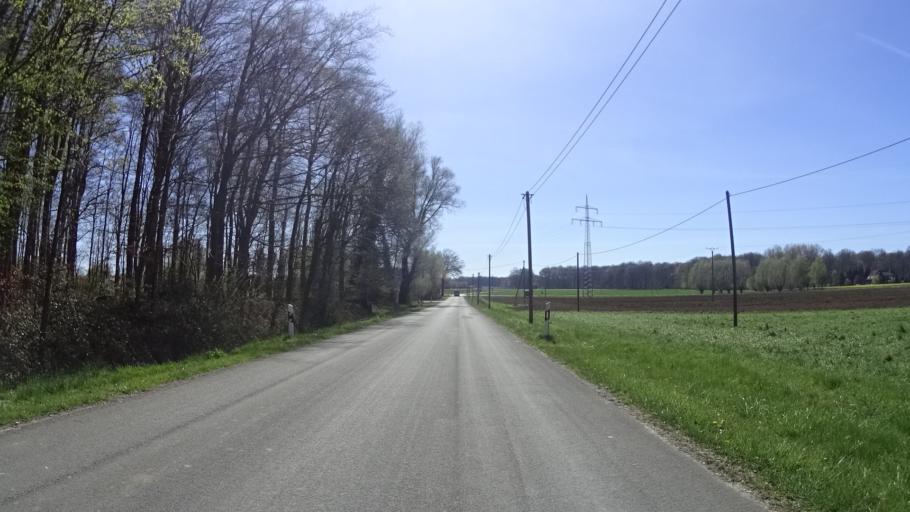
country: DE
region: North Rhine-Westphalia
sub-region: Regierungsbezirk Munster
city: Dulmen
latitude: 51.8175
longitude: 7.3502
